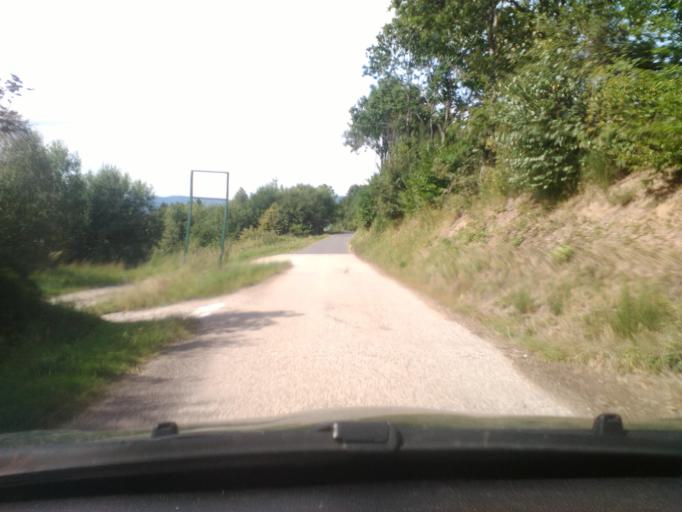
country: FR
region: Lorraine
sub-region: Departement des Vosges
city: Fraize
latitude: 48.2105
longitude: 7.0219
